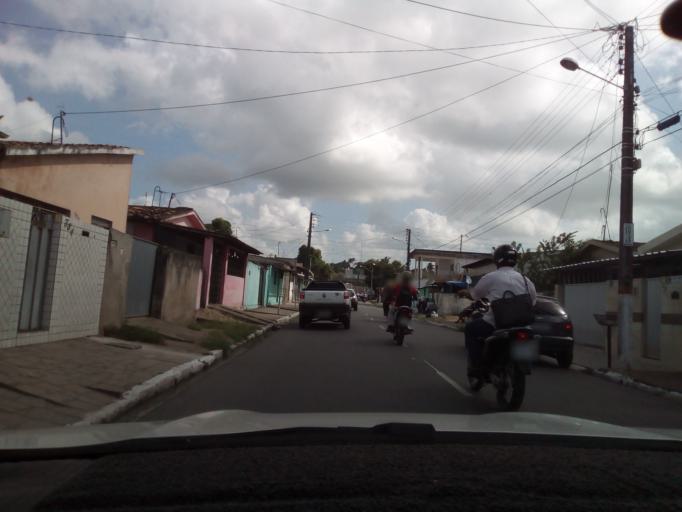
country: BR
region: Paraiba
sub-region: Bayeux
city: Bayeux
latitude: -7.1295
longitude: -34.9322
